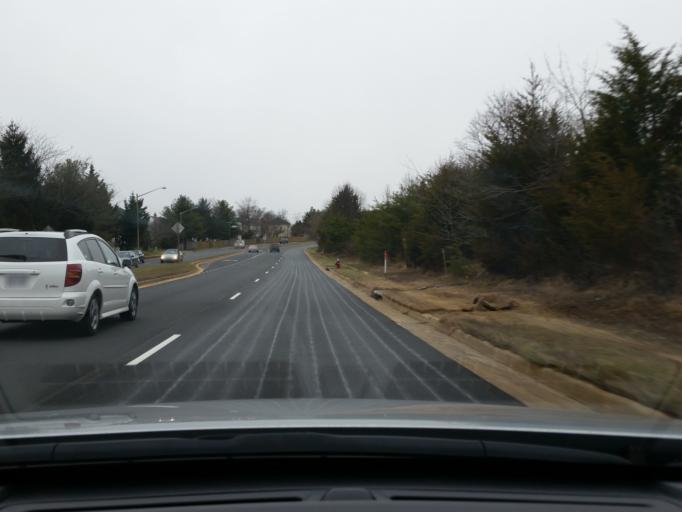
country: US
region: Virginia
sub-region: Fairfax County
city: Herndon
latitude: 38.9481
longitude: -77.3879
